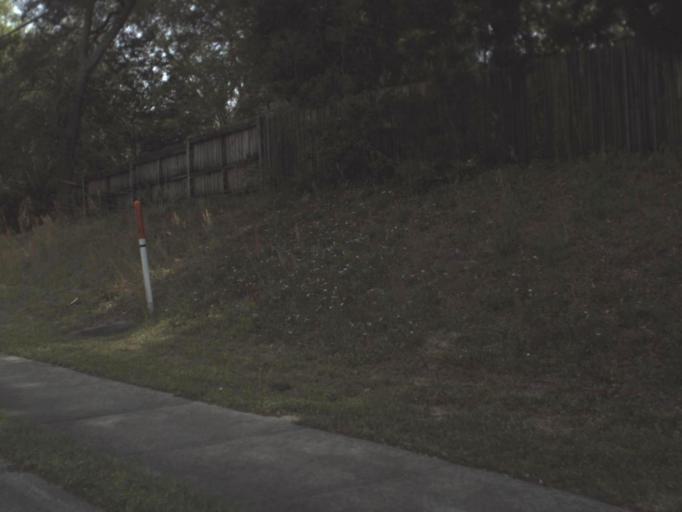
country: US
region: Florida
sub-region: Okaloosa County
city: Niceville
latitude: 30.5101
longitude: -86.4437
